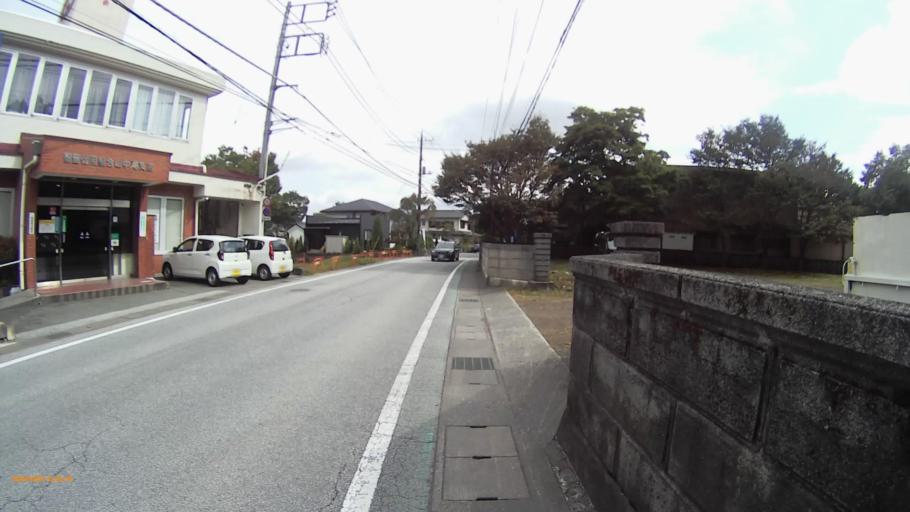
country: JP
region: Shizuoka
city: Gotemba
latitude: 35.4219
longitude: 138.8496
